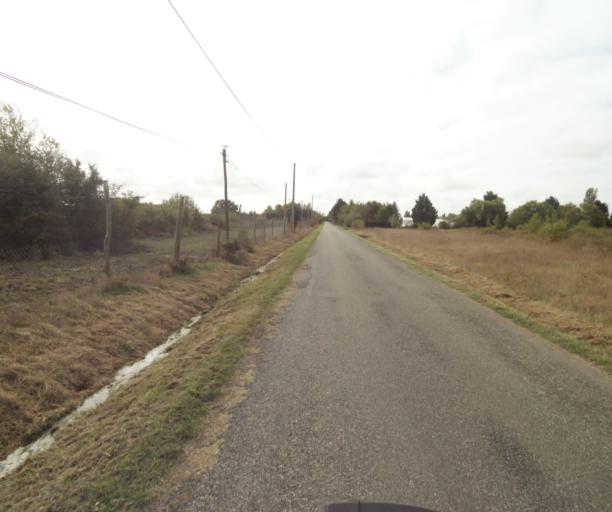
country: FR
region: Midi-Pyrenees
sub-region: Departement du Tarn-et-Garonne
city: Finhan
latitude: 43.9263
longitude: 1.2468
